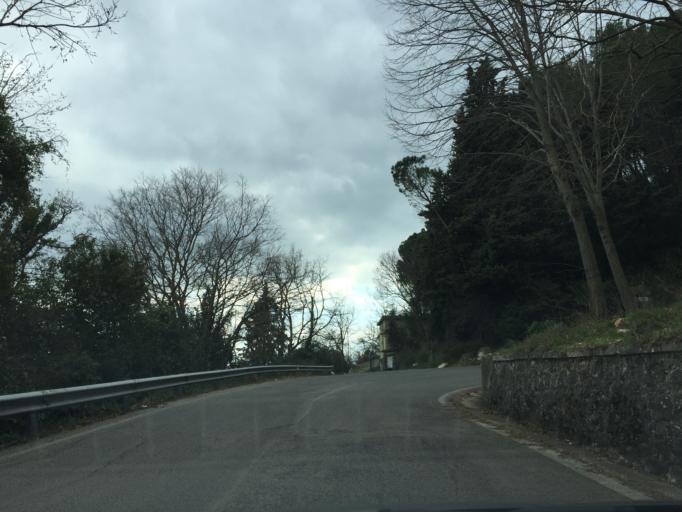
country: IT
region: Latium
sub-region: Provincia di Frosinone
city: Cassino
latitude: 41.4887
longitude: 13.8205
